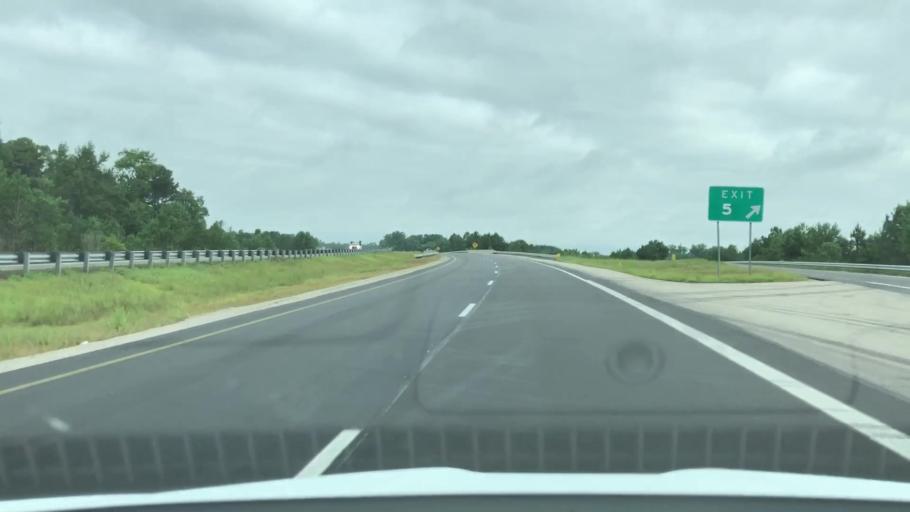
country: US
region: North Carolina
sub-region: Wilson County
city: Lucama
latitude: 35.6653
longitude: -77.9558
